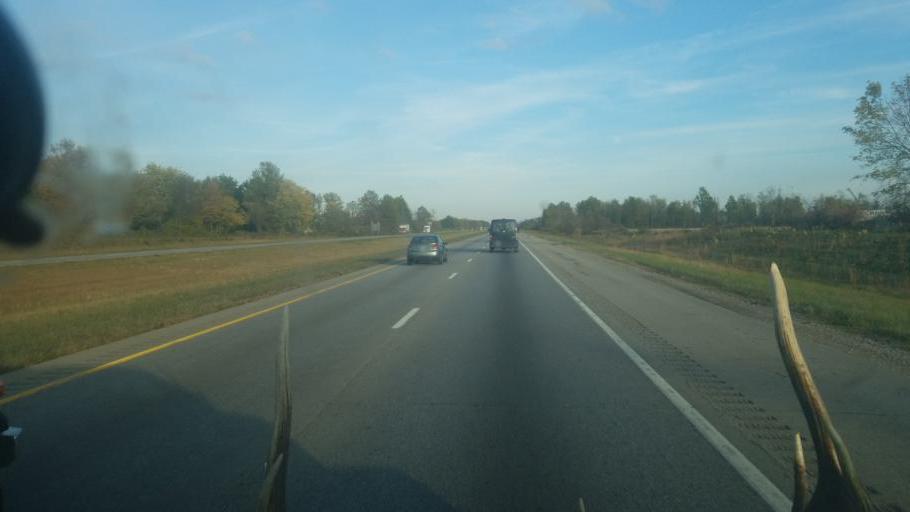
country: US
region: Ohio
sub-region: Licking County
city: Etna
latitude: 39.9506
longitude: -82.7210
